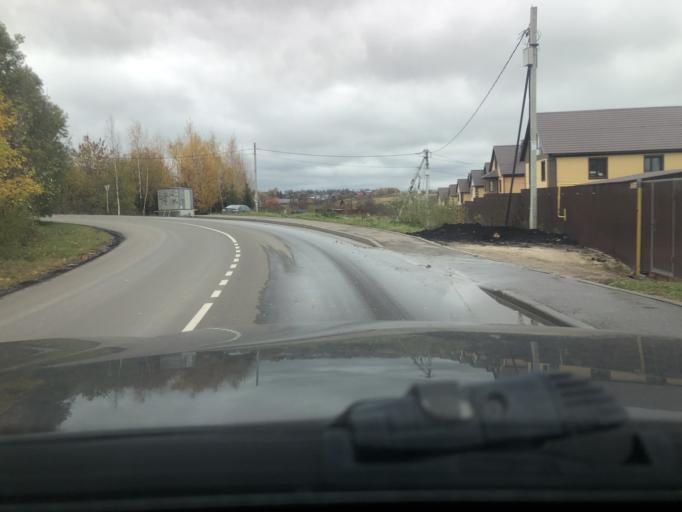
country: RU
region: Moskovskaya
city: Sergiyev Posad
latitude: 56.3058
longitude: 38.1016
